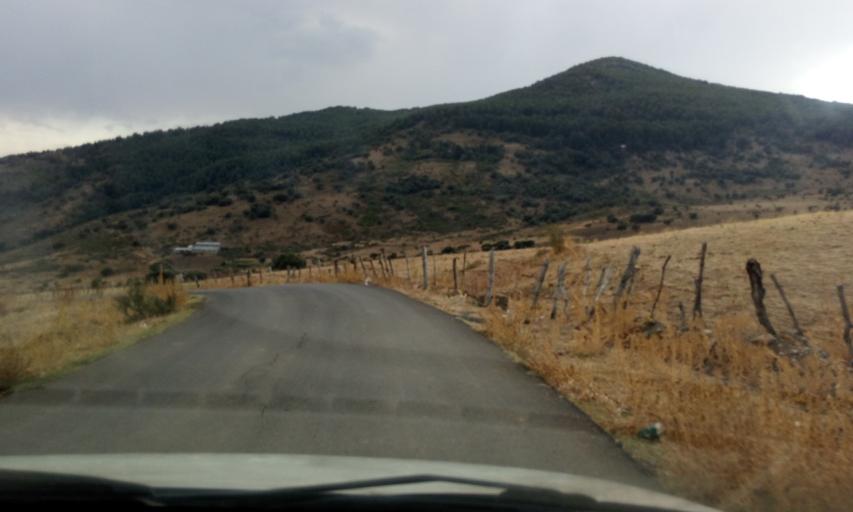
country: DZ
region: Tizi Ouzou
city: Chemini
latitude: 36.6135
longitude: 4.5584
